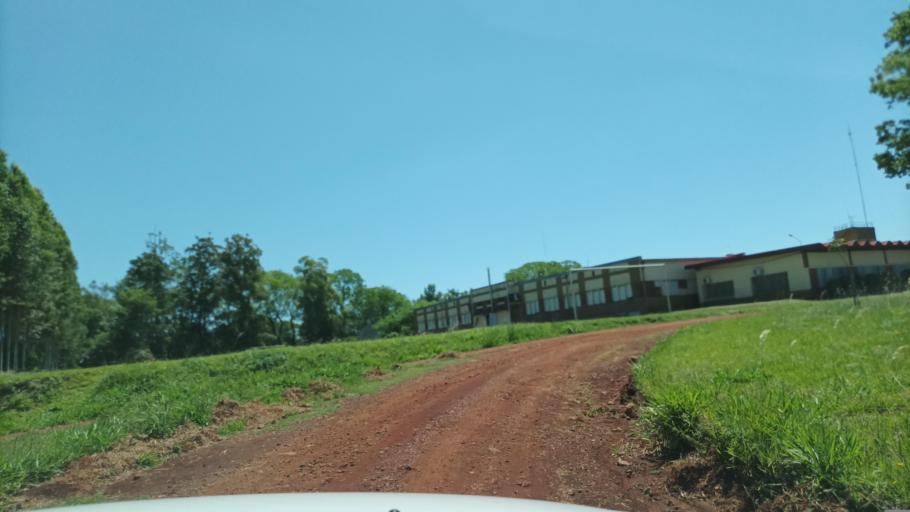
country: AR
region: Misiones
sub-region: Departamento de Apostoles
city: San Jose
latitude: -27.7922
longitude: -55.7147
